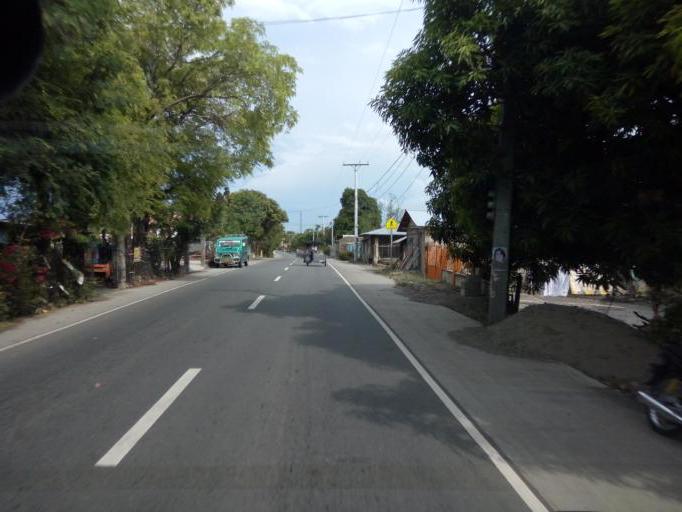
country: PH
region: Central Luzon
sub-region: Province of Nueva Ecija
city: Parista
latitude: 15.8181
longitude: 120.9575
